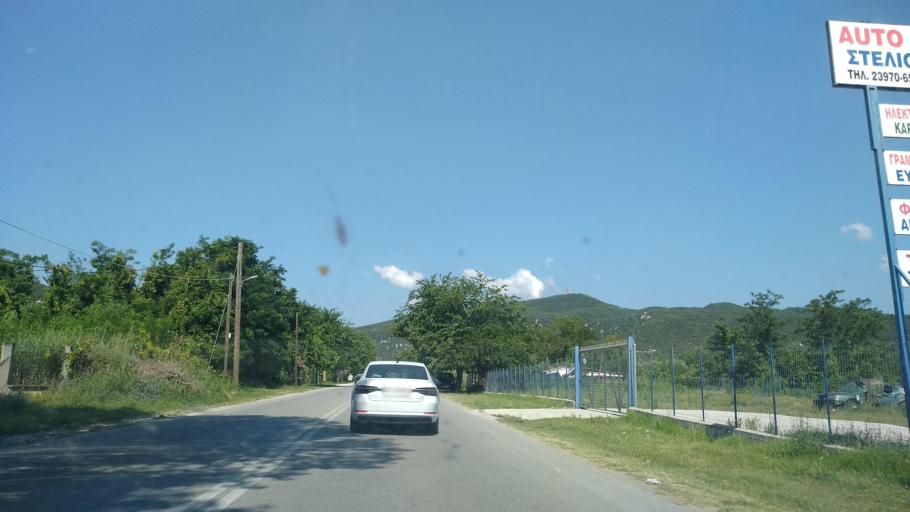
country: GR
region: Central Macedonia
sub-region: Nomos Thessalonikis
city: Stavros
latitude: 40.6682
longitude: 23.6793
